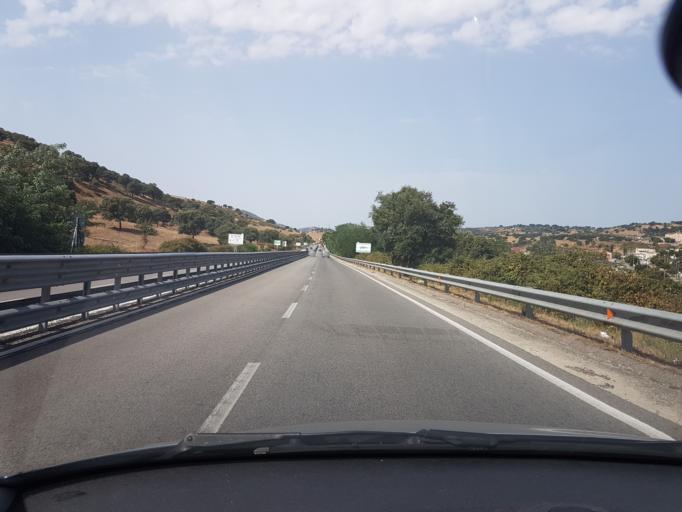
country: IT
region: Sardinia
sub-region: Provincia di Nuoro
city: Nuoro
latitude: 40.3225
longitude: 9.2726
